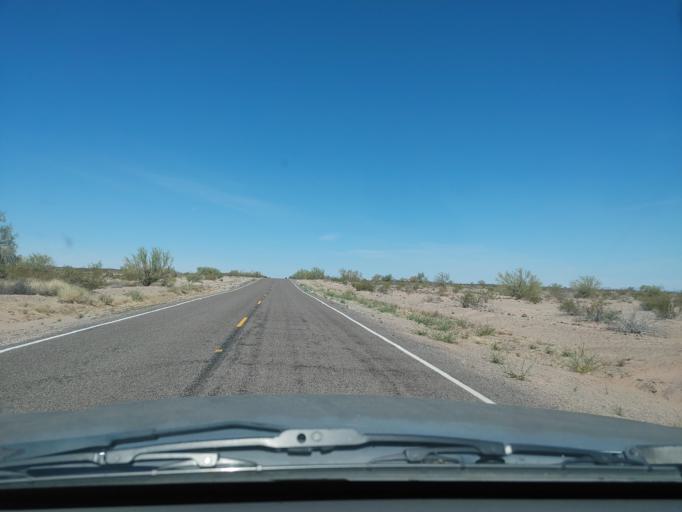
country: US
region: Arizona
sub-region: Maricopa County
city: Gila Bend
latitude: 32.8819
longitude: -113.2281
